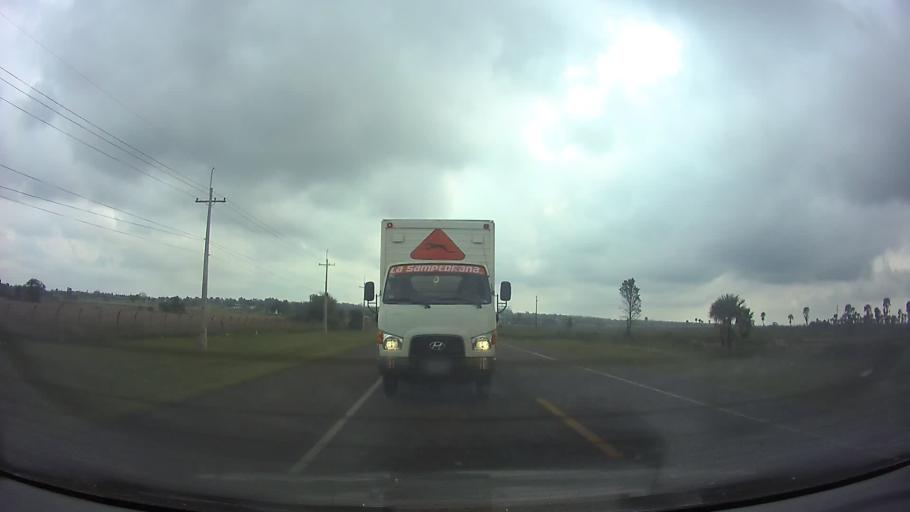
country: PY
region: Cordillera
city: Arroyos y Esteros
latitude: -25.0636
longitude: -57.1913
